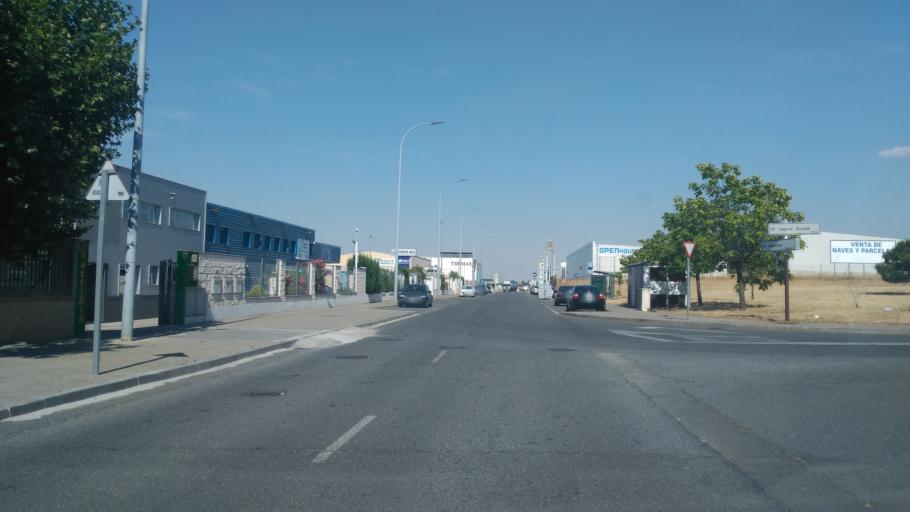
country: ES
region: Castille and Leon
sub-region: Provincia de Salamanca
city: Carbajosa de la Sagrada
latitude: 40.9389
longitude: -5.6642
